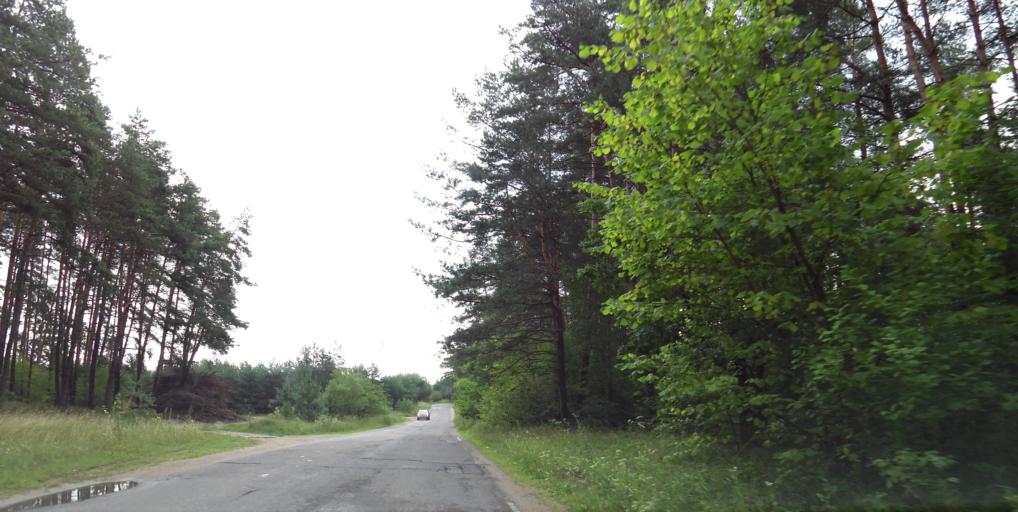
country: LT
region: Vilnius County
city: Pilaite
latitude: 54.6967
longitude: 25.2005
